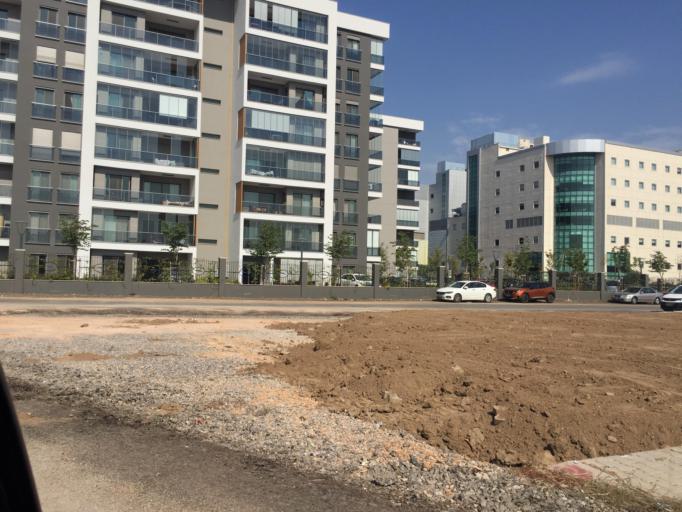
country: TR
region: Izmir
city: Karsiyaka
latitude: 38.4887
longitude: 27.0502
